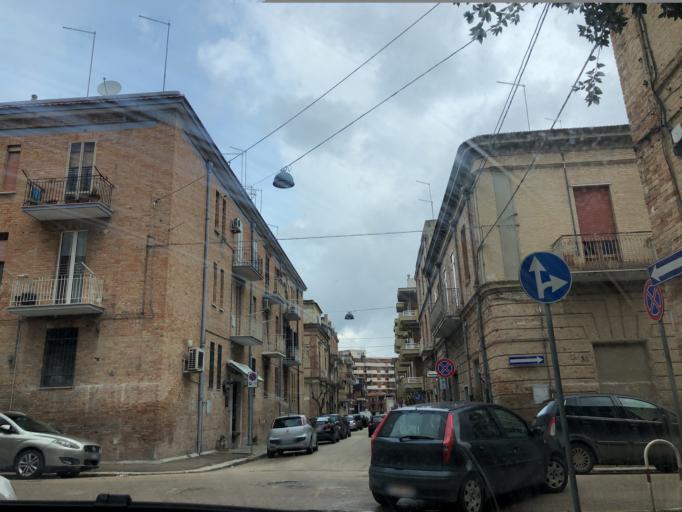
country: IT
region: Apulia
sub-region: Provincia di Foggia
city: Lucera
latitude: 41.5071
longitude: 15.3301
